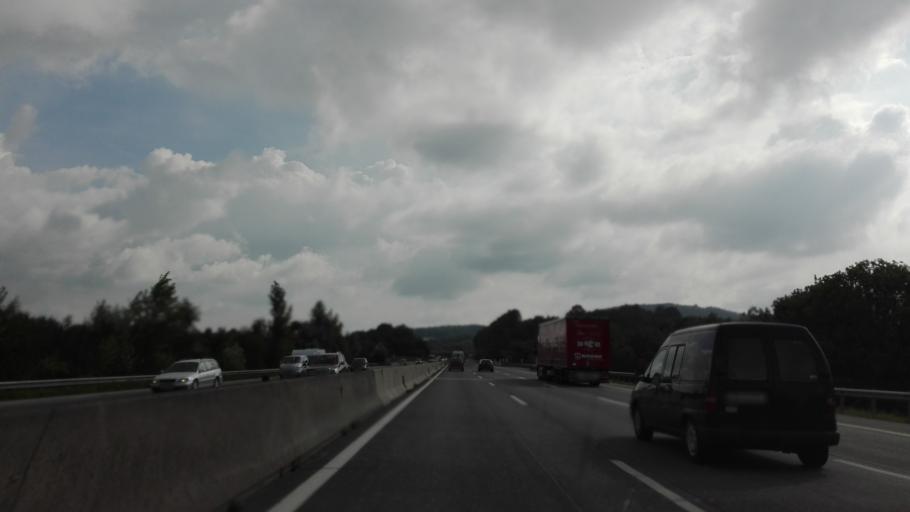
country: AT
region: Lower Austria
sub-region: Politischer Bezirk Melk
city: Erlauf
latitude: 48.1680
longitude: 15.1702
